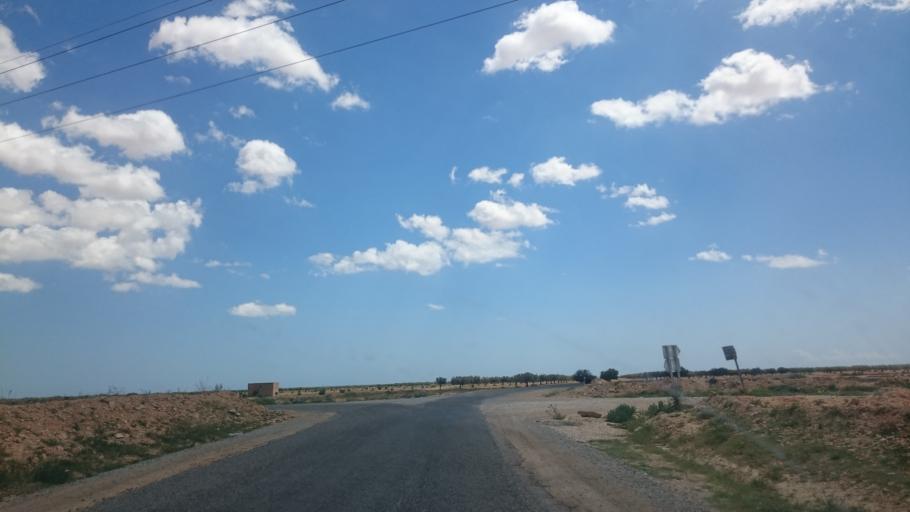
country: TN
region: Safaqis
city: Sfax
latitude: 34.6903
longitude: 10.5637
